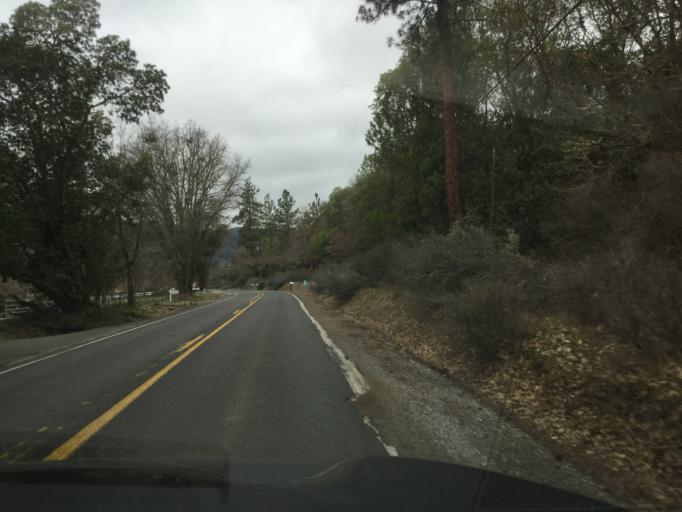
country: US
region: Oregon
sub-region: Jackson County
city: Gold Hill
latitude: 42.3966
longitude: -123.0063
